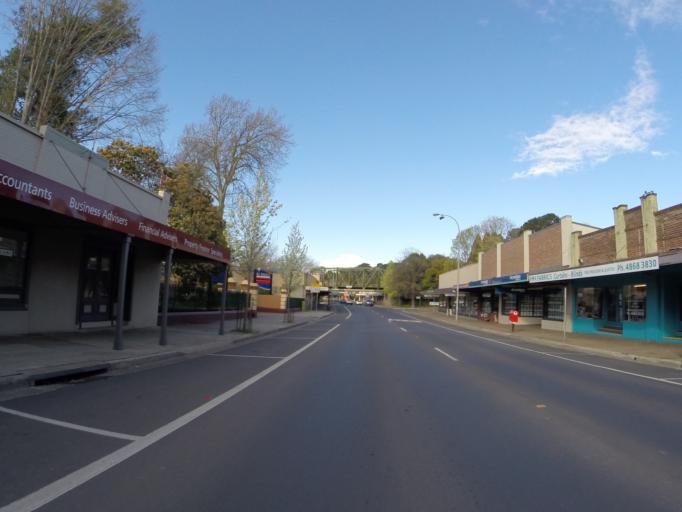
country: AU
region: New South Wales
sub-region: Wingecarribee
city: Moss Vale
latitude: -34.5512
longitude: 150.3685
